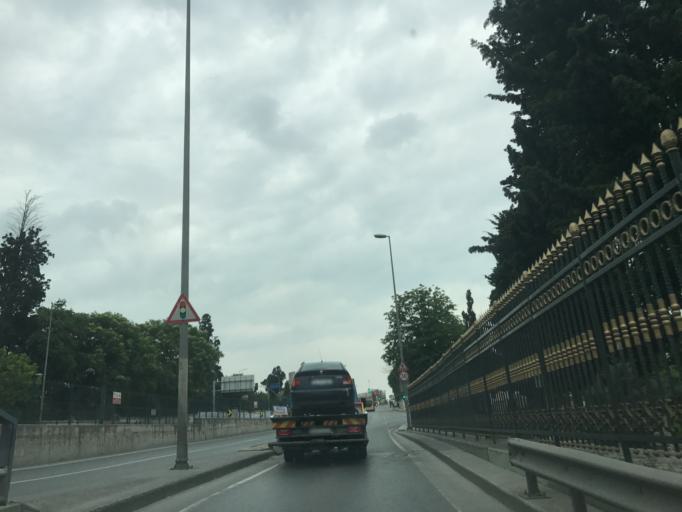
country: TR
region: Istanbul
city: Istanbul
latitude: 41.0326
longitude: 28.9325
